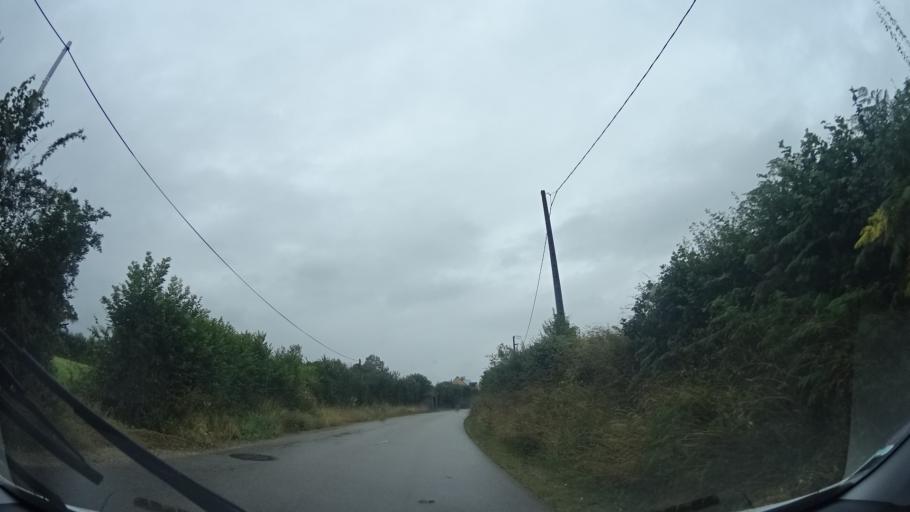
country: FR
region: Lower Normandy
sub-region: Departement de la Manche
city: Urville-Nacqueville
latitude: 49.5999
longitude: -1.7472
